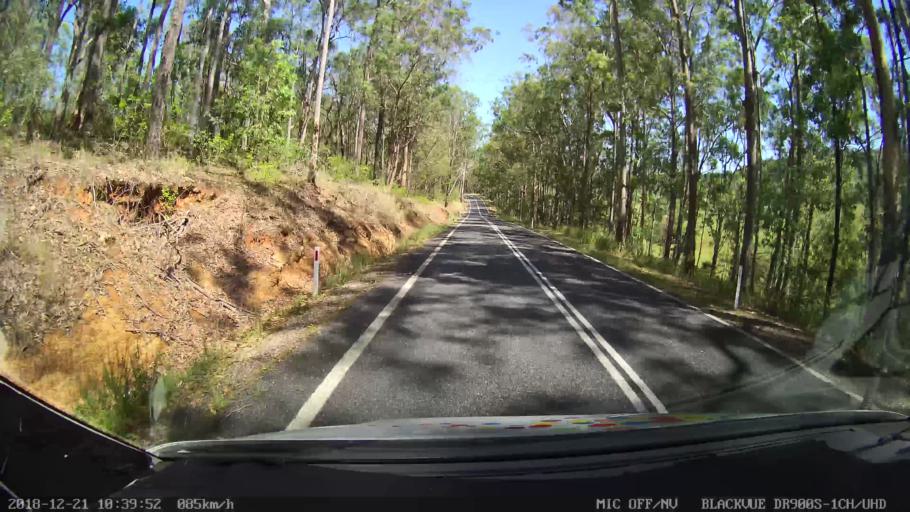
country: AU
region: New South Wales
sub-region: Clarence Valley
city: Gordon
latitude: -29.6046
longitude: 152.5920
